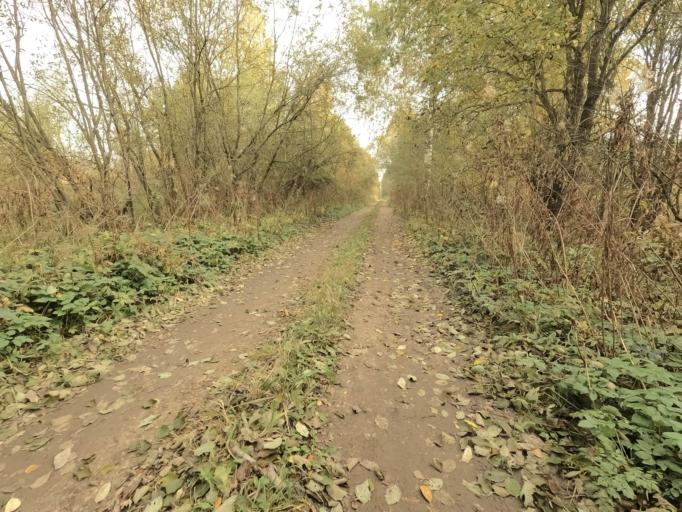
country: RU
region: Novgorod
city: Pankovka
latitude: 58.8798
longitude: 30.8129
